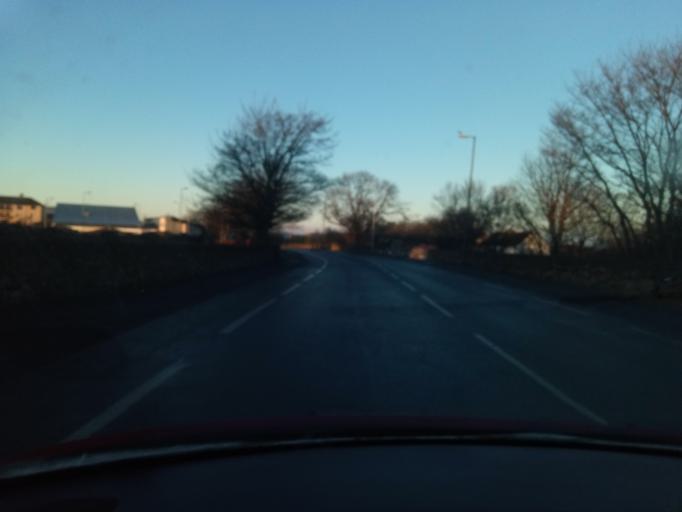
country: GB
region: Scotland
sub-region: East Lothian
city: Musselburgh
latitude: 55.9439
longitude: -3.0204
